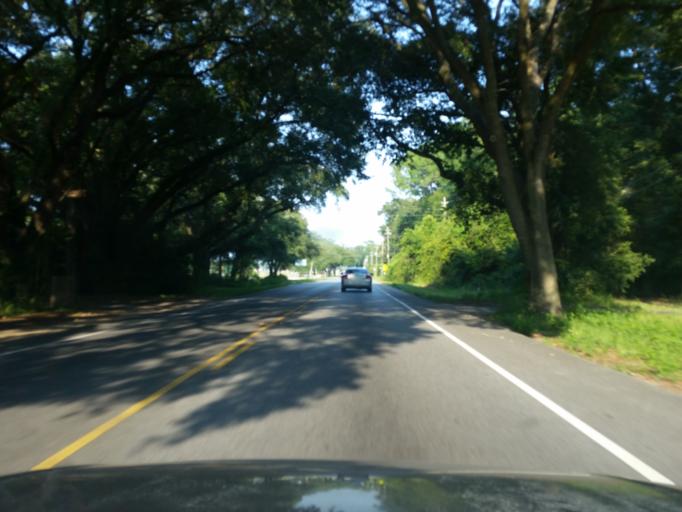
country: US
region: Florida
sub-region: Escambia County
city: Bellview
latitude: 30.4866
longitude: -87.3038
